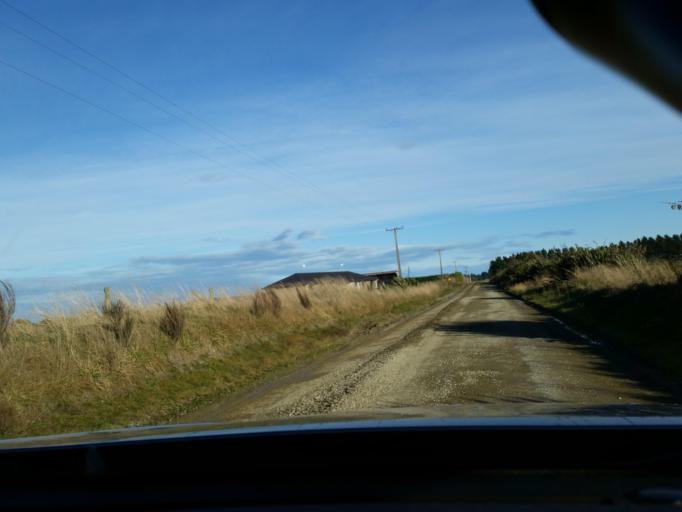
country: NZ
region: Southland
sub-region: Southland District
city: Winton
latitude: -46.2482
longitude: 168.4674
